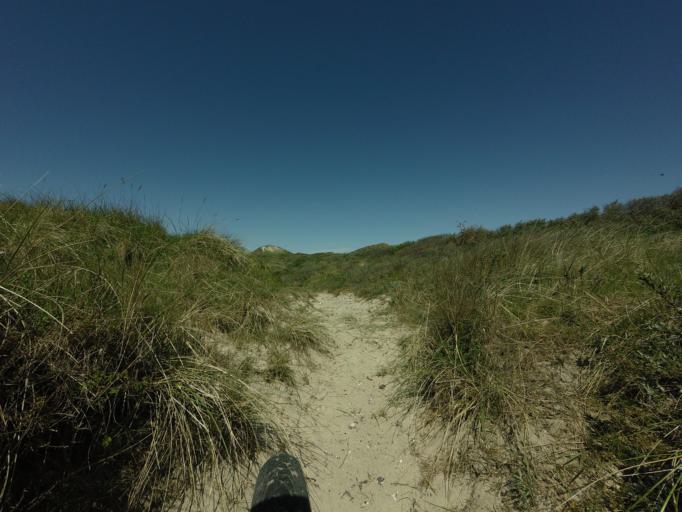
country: DK
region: North Denmark
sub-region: Jammerbugt Kommune
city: Pandrup
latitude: 57.2334
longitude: 9.5566
